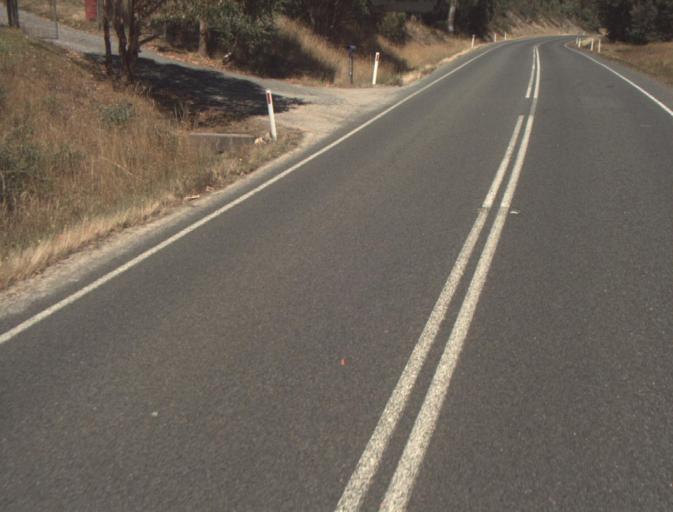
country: AU
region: Tasmania
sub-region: Dorset
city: Scottsdale
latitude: -41.3156
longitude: 147.3671
